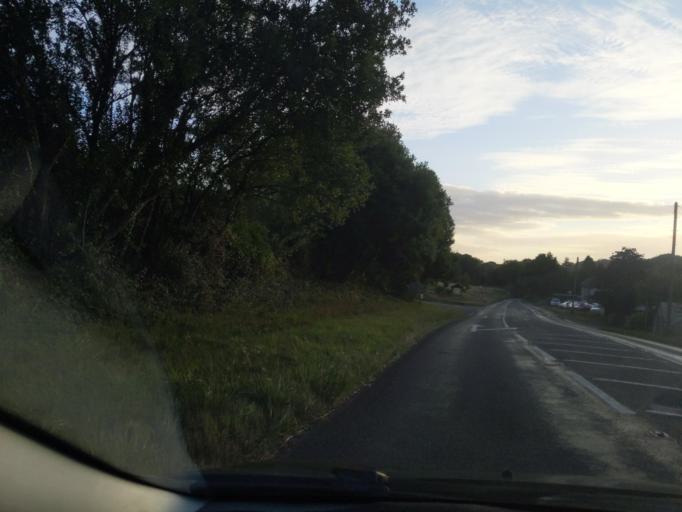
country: GB
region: England
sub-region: Devon
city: Yealmpton
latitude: 50.3515
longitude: -3.9777
